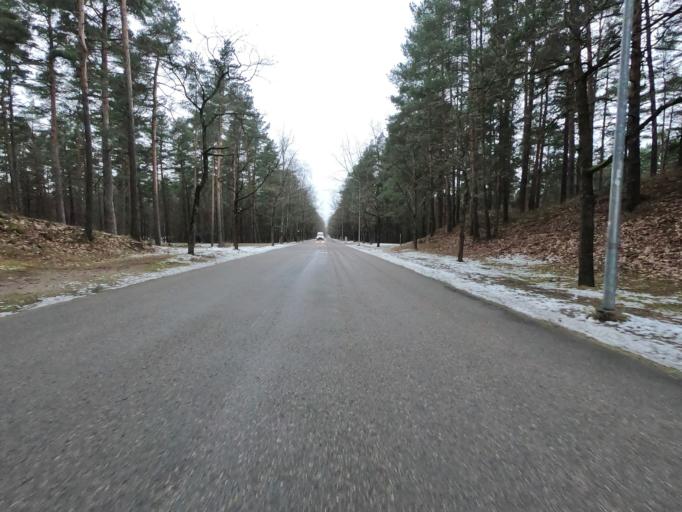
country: LV
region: Riga
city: Jaunciems
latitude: 57.0159
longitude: 24.1461
